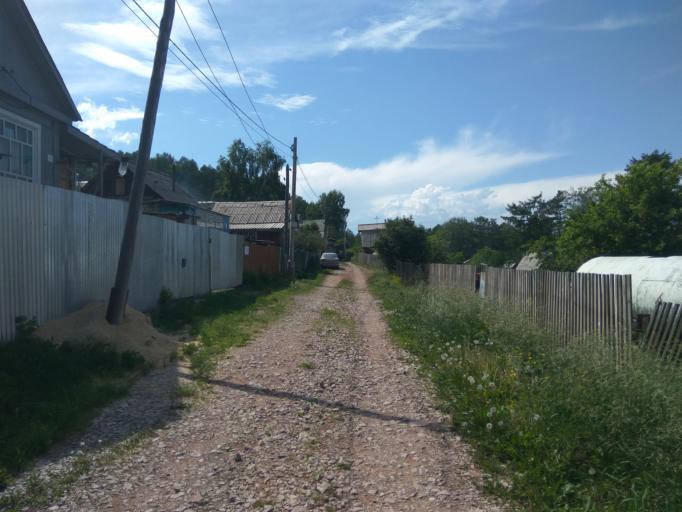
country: RU
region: Krasnoyarskiy
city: Krasnoyarsk
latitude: 55.9649
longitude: 92.8656
